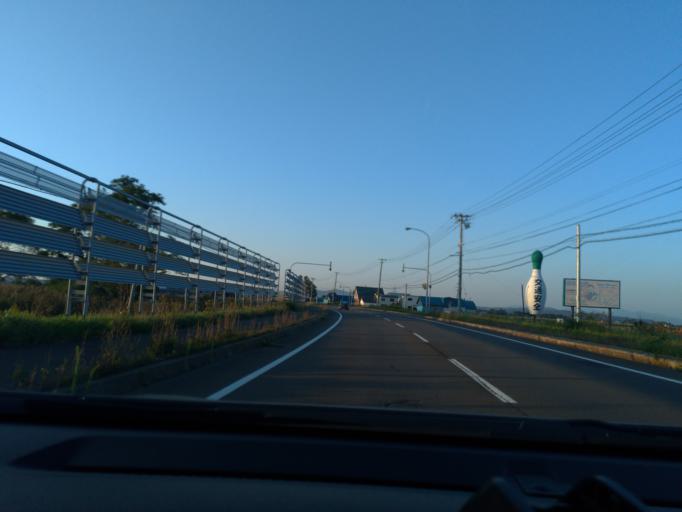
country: JP
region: Hokkaido
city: Tobetsu
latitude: 43.1905
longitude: 141.5247
